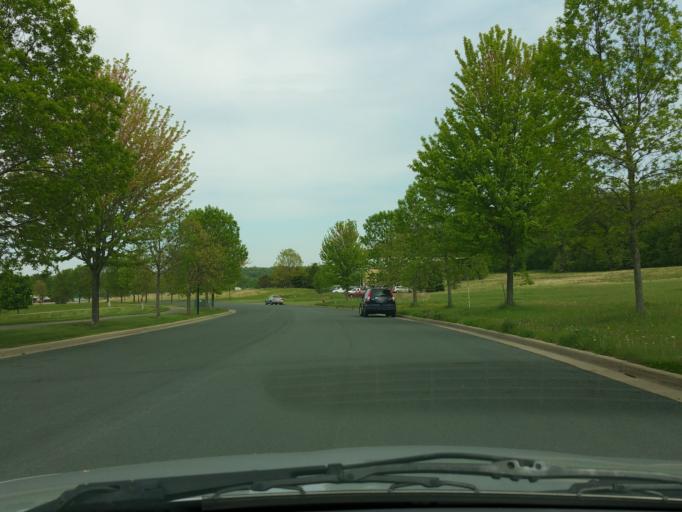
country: US
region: Wisconsin
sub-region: Pierce County
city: River Falls
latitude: 44.8843
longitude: -92.6317
